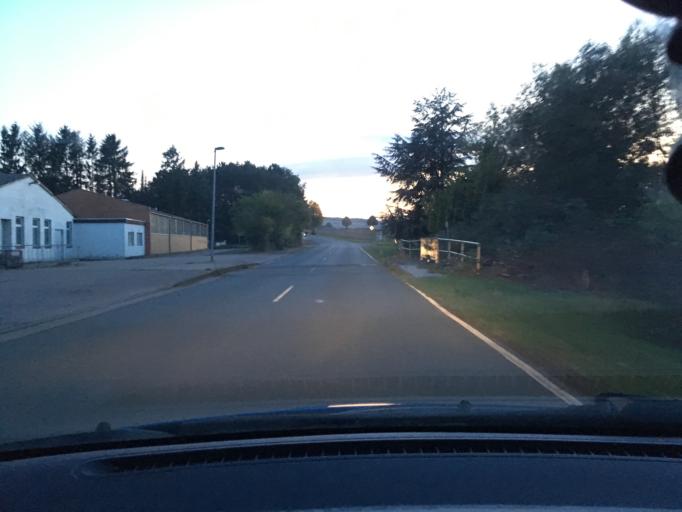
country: DE
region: Lower Saxony
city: Messenkamp
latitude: 52.2574
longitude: 9.3714
